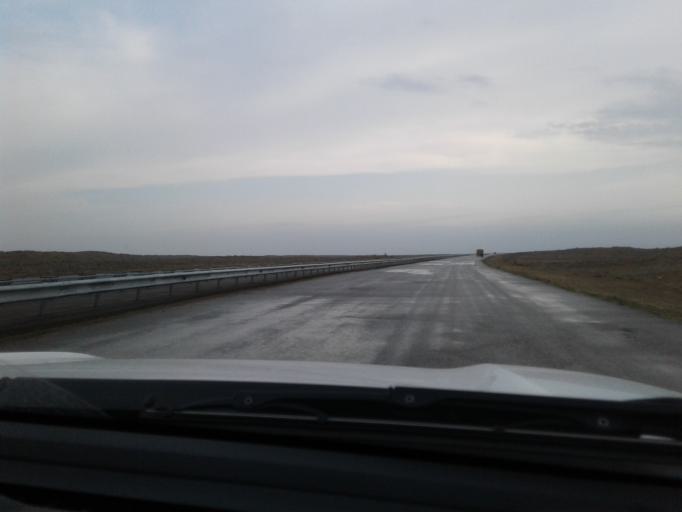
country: TM
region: Ahal
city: Abadan
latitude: 38.4713
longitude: 58.5058
